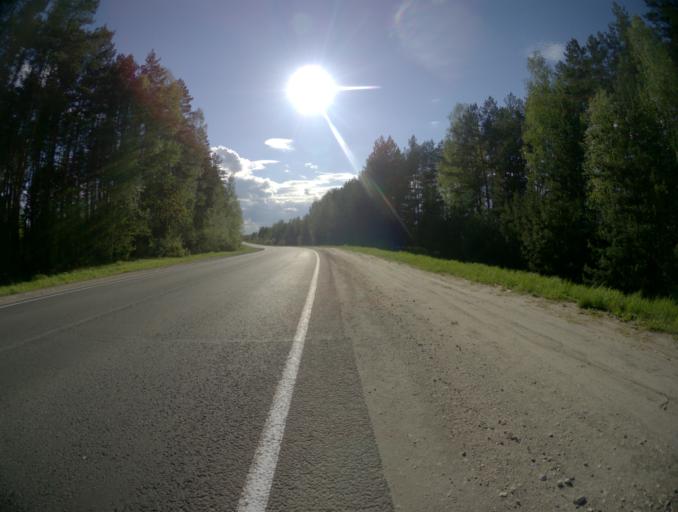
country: RU
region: Rjazan
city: Spas-Klepiki
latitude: 55.1511
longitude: 40.2693
